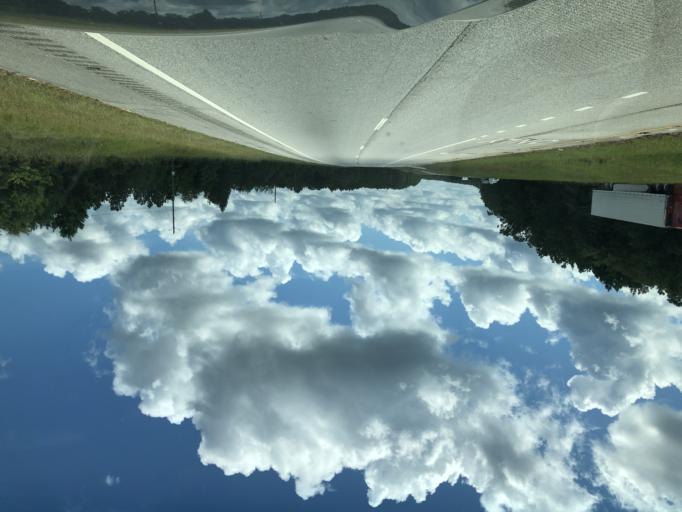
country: US
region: Alabama
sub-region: Russell County
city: Ladonia
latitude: 32.2248
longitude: -85.1710
